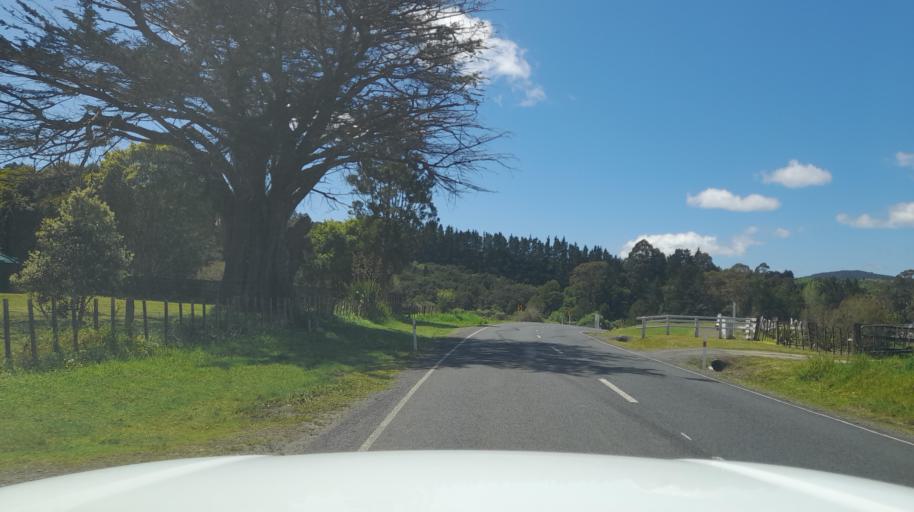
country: NZ
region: Northland
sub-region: Far North District
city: Taipa
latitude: -35.0985
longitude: 173.4880
